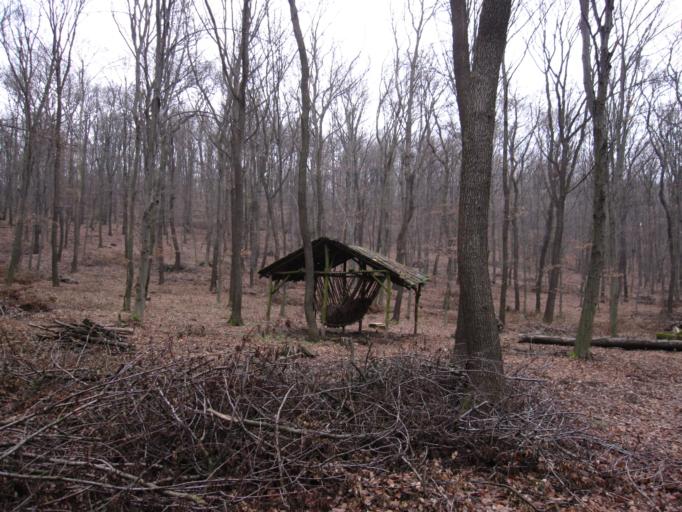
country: HU
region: Pest
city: Piliscsaba
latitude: 47.6604
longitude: 18.8501
